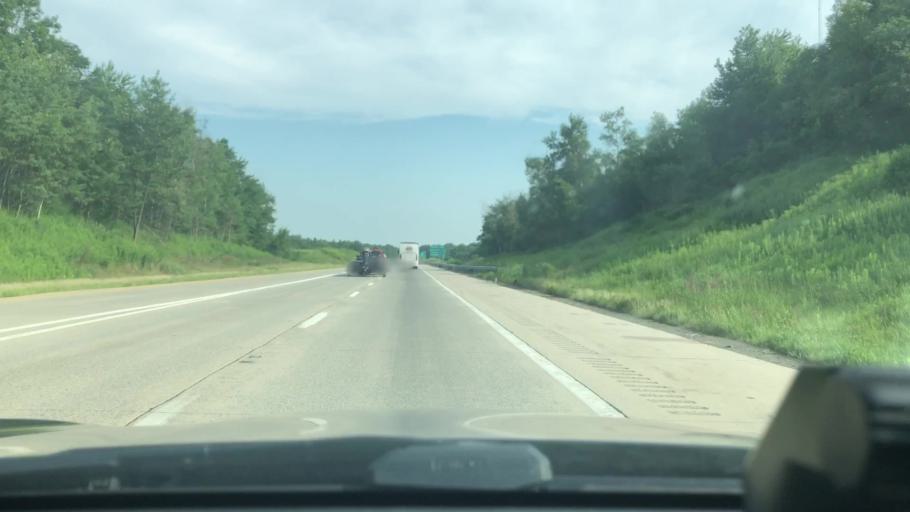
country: US
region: Pennsylvania
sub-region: Monroe County
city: Emerald Lakes
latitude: 41.0769
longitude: -75.3941
